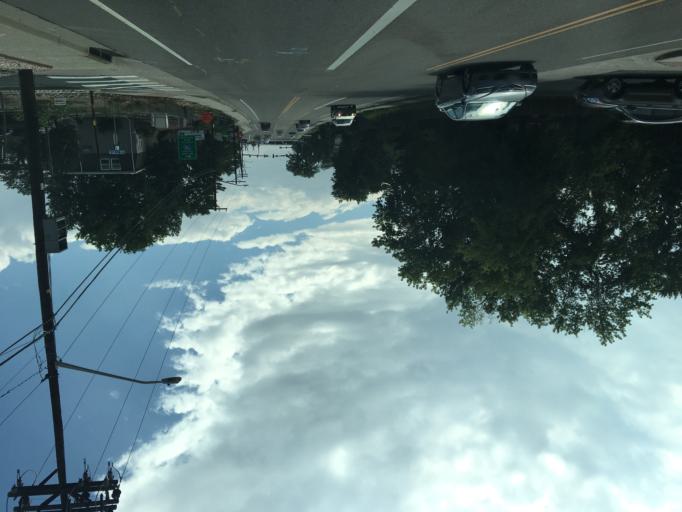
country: US
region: Colorado
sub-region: Jefferson County
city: Applewood
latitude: 39.7619
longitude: -105.1372
